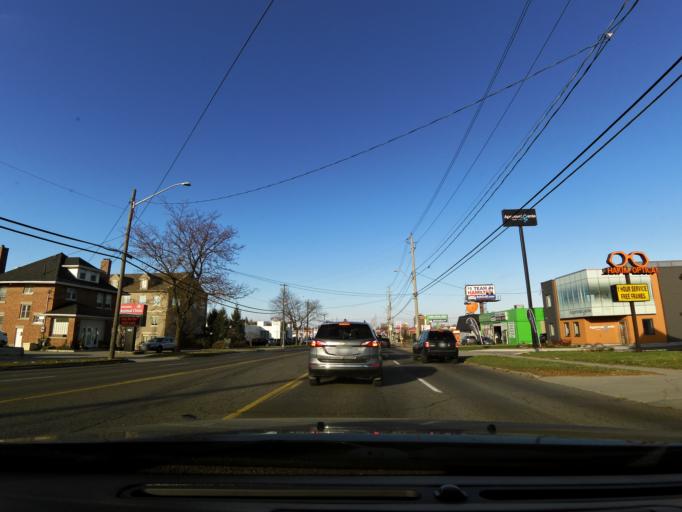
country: CA
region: Ontario
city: Hamilton
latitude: 43.2236
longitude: -79.8838
